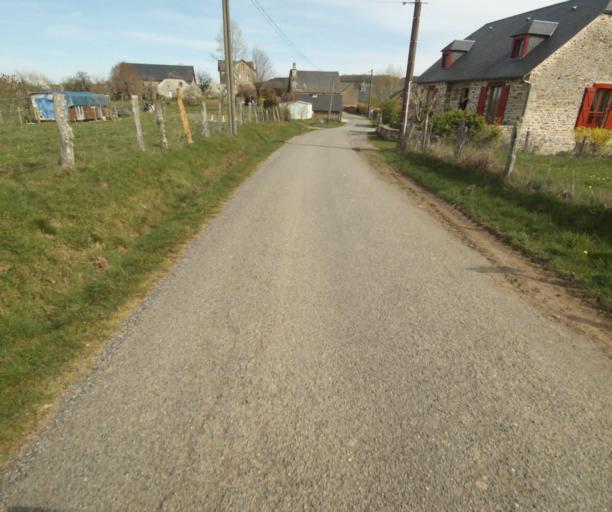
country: FR
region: Limousin
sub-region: Departement de la Correze
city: Correze
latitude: 45.3859
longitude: 1.8225
